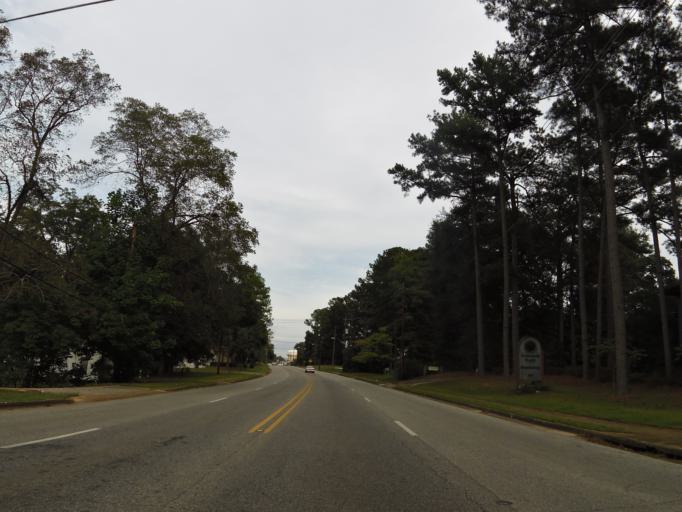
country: US
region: Alabama
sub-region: Monroe County
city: Monroeville
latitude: 31.5260
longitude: -87.3329
